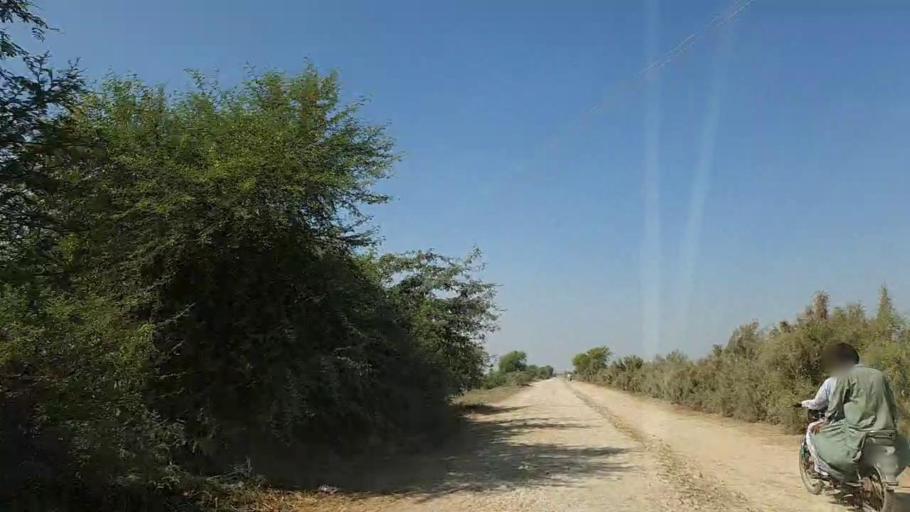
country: PK
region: Sindh
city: Chuhar Jamali
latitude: 24.4200
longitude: 68.0147
